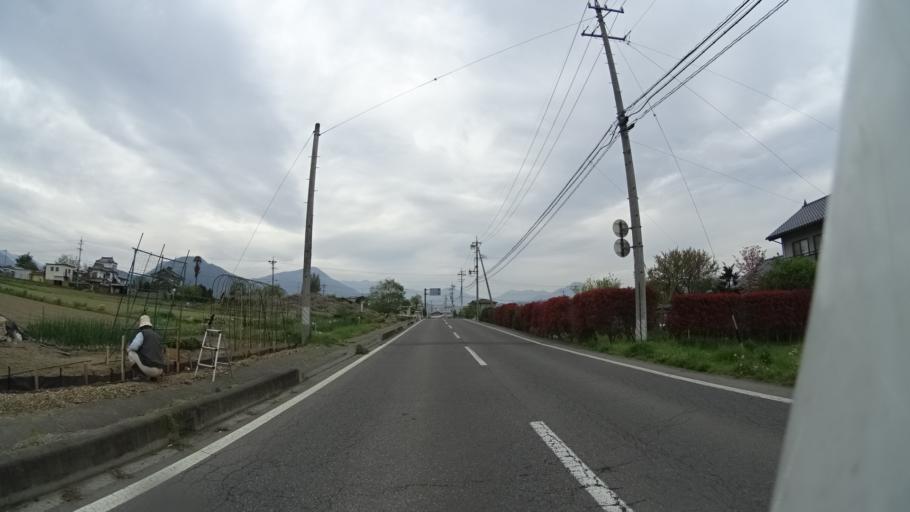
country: JP
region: Nagano
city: Kamimaruko
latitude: 36.3493
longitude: 138.1987
